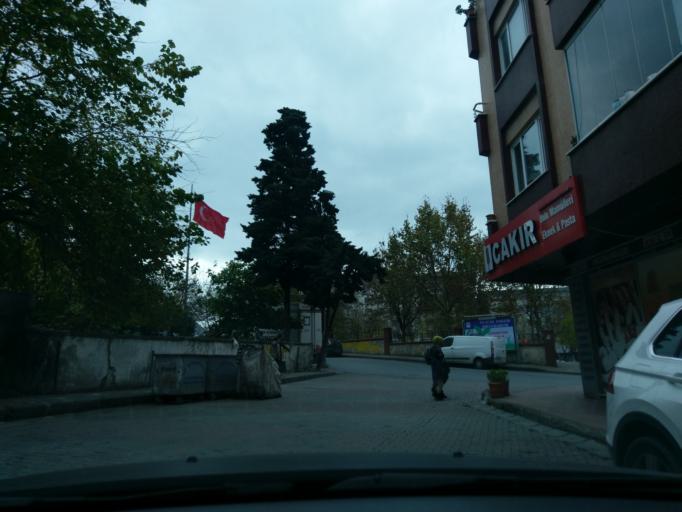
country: TR
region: Istanbul
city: Bahcelievler
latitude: 41.0155
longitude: 28.8532
